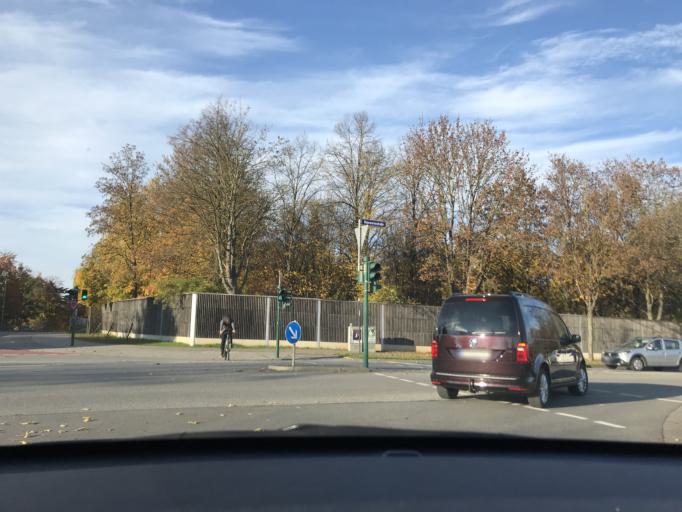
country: DE
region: Bavaria
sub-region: Upper Palatinate
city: Regensburg
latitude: 48.9950
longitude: 12.1116
